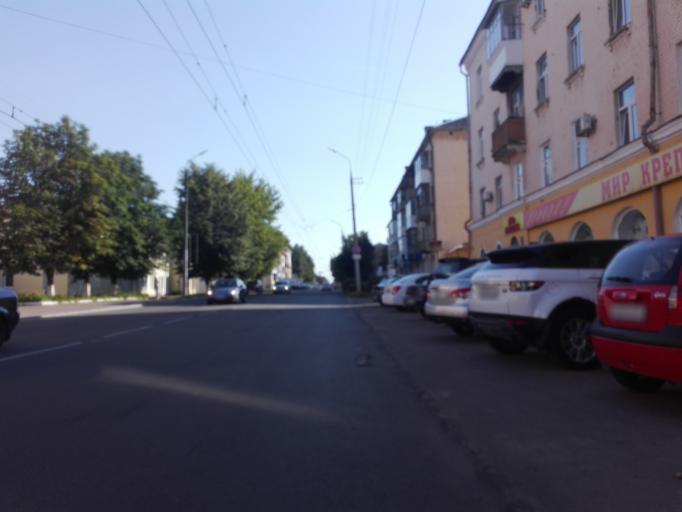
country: RU
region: Orjol
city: Orel
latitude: 52.9776
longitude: 36.0659
